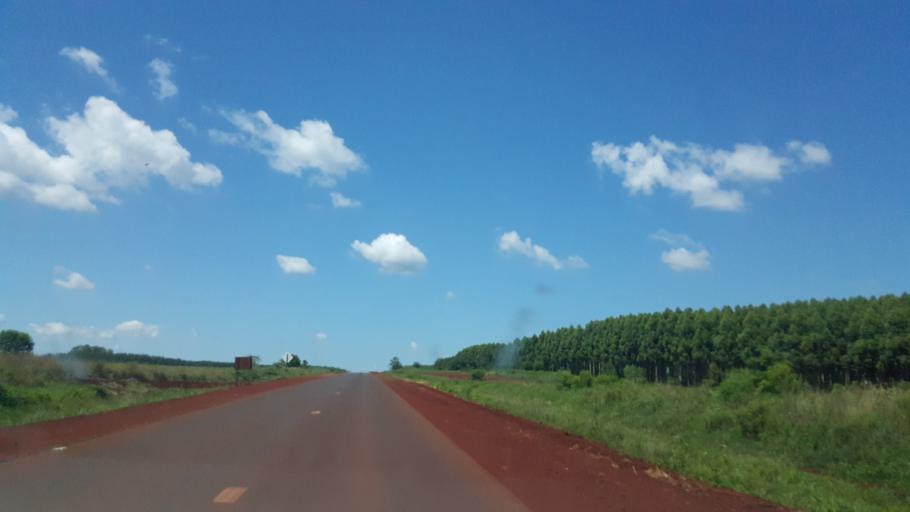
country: AR
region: Corrientes
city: Santo Tome
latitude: -28.3498
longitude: -55.9356
